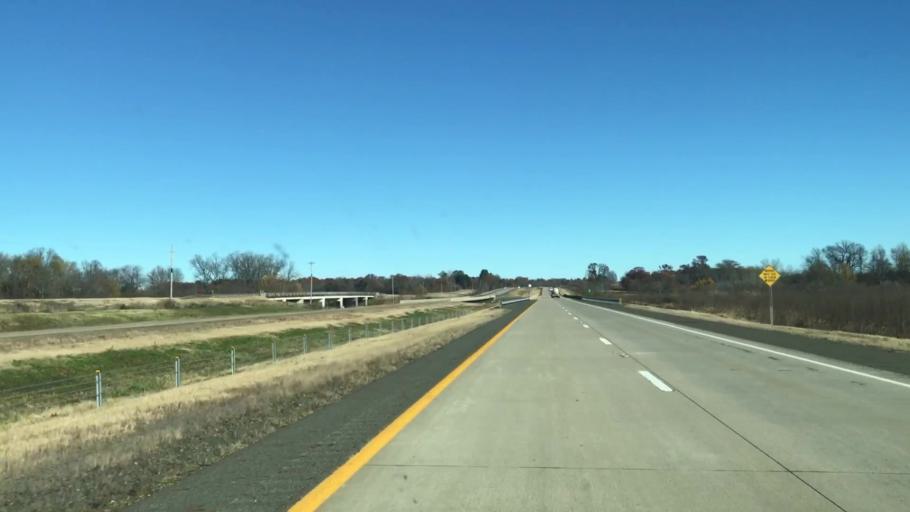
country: US
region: Texas
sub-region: Cass County
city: Queen City
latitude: 33.1464
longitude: -93.8917
